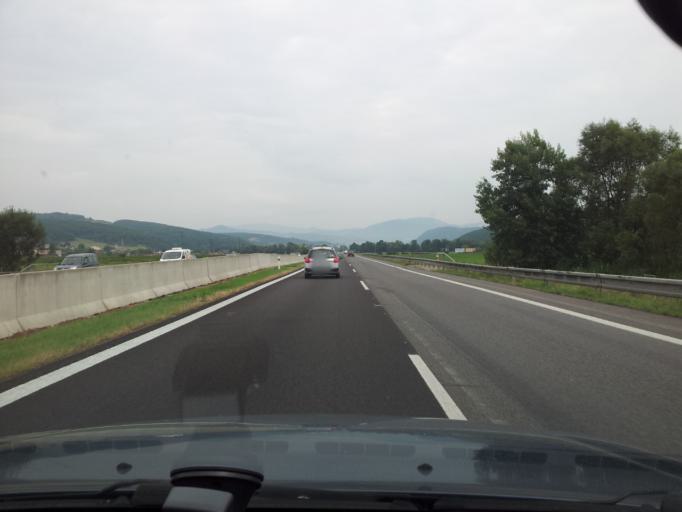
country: SK
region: Banskobystricky
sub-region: Okres Banska Bystrica
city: Banska Bystrica
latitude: 48.6726
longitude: 19.1327
